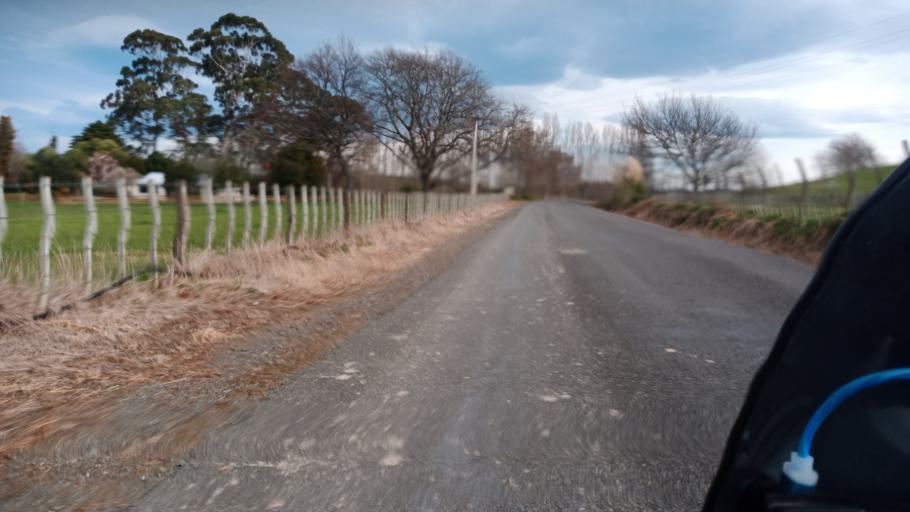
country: NZ
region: Hawke's Bay
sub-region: Wairoa District
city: Wairoa
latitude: -38.9733
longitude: 177.4317
